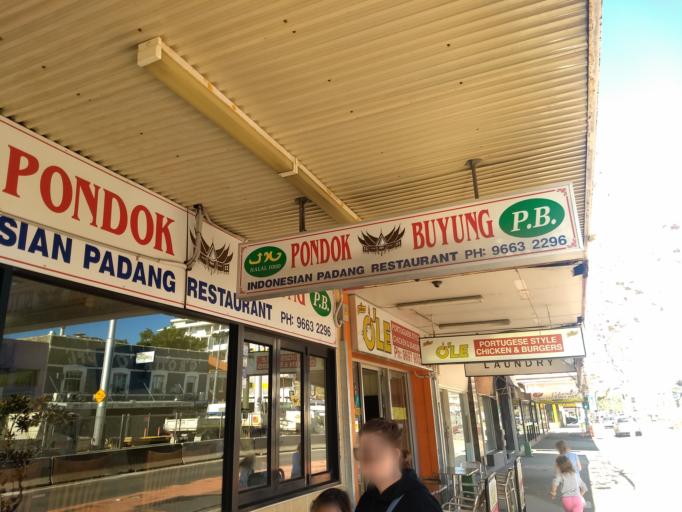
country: AU
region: New South Wales
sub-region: Randwick
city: Kensington
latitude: -33.9083
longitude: 151.2236
